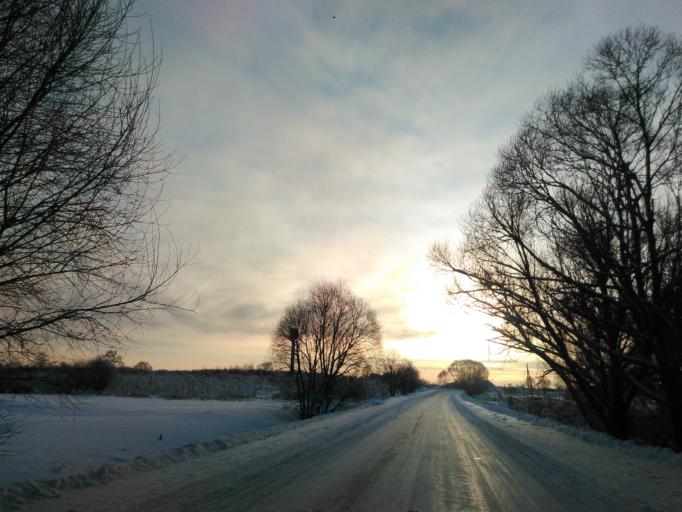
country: RU
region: Tverskaya
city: Zavidovo
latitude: 56.6320
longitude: 36.6172
